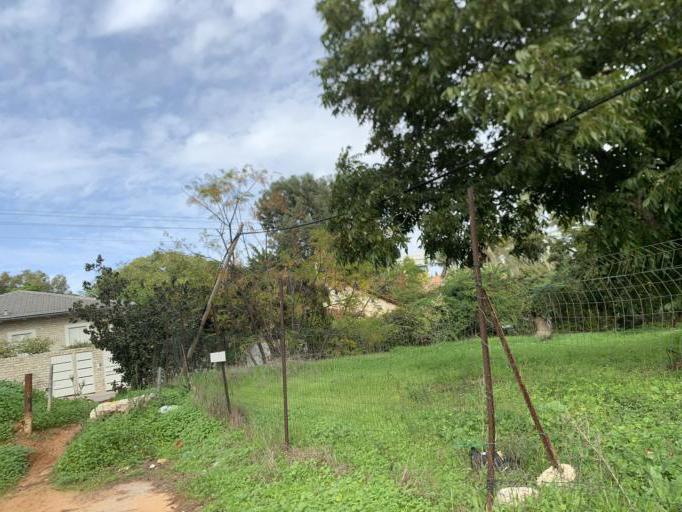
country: IL
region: Central District
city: Hod HaSharon
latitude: 32.1543
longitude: 34.9009
